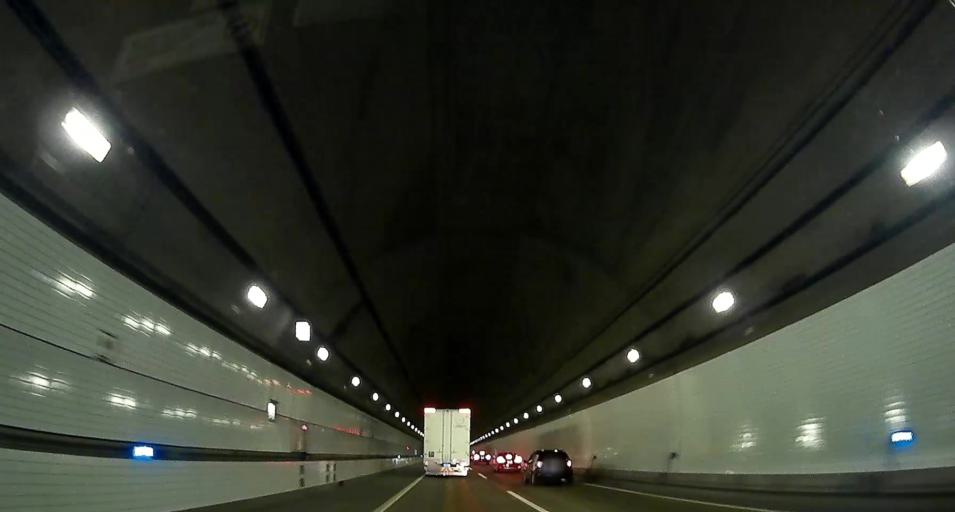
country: JP
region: Chiba
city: Kisarazu
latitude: 35.4710
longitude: 139.8640
